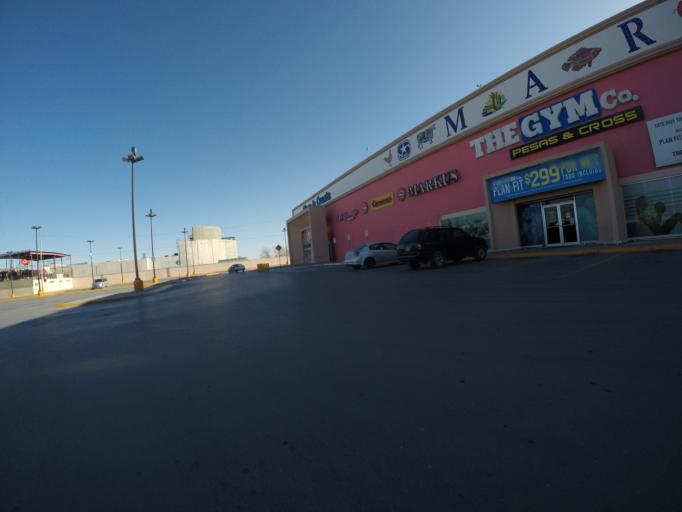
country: MX
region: Chihuahua
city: Ciudad Juarez
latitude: 31.6762
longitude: -106.4234
